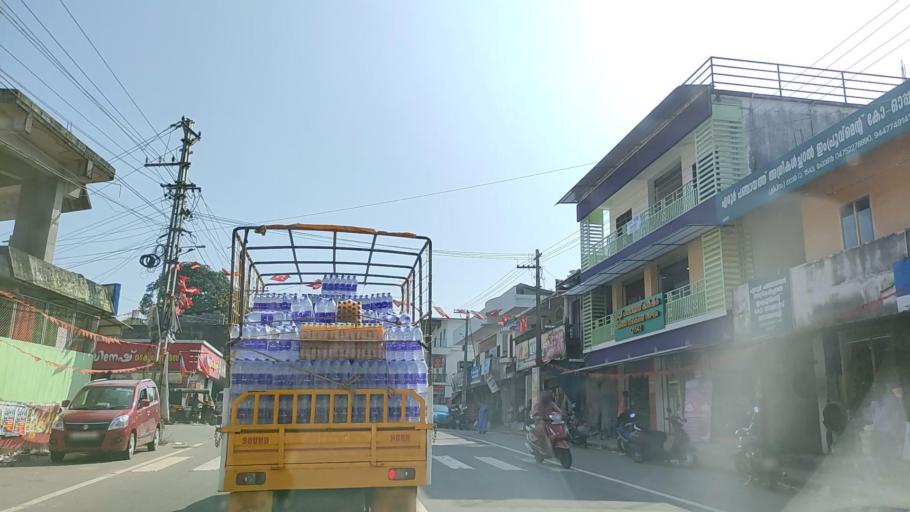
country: IN
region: Kerala
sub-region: Kollam
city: Punalur
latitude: 8.9358
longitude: 76.9459
